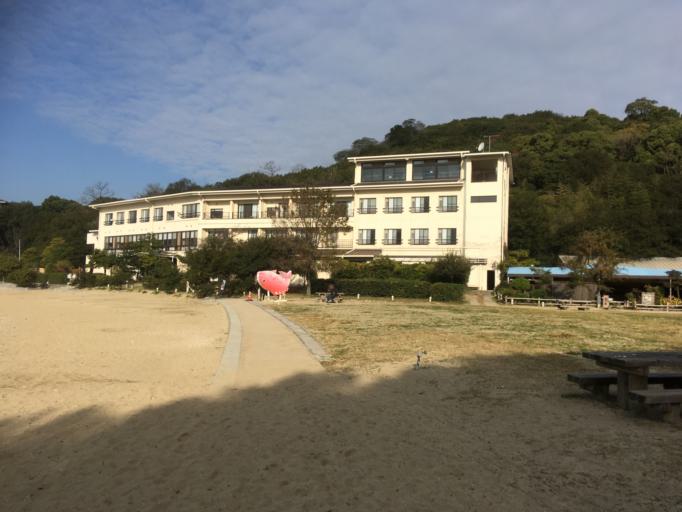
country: JP
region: Hiroshima
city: Fukuyama
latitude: 34.3833
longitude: 133.3918
